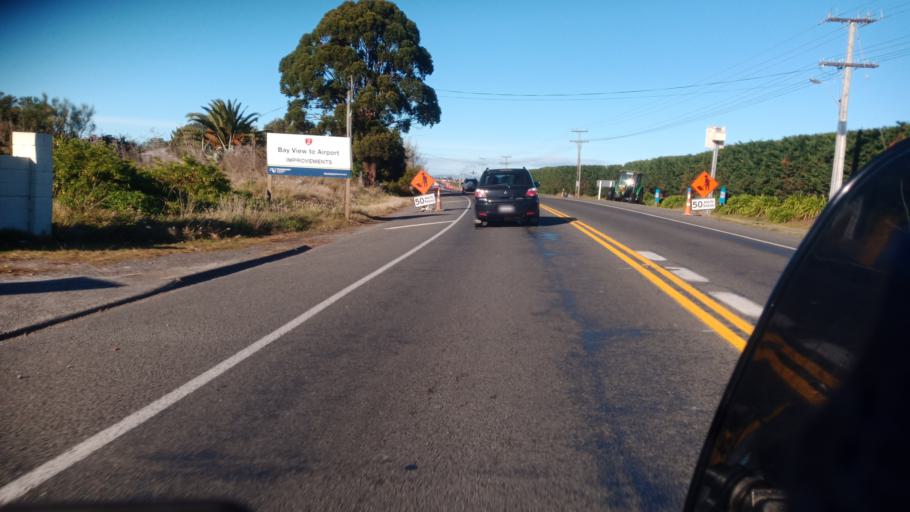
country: NZ
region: Hawke's Bay
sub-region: Napier City
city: Napier
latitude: -39.4377
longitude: 176.8702
